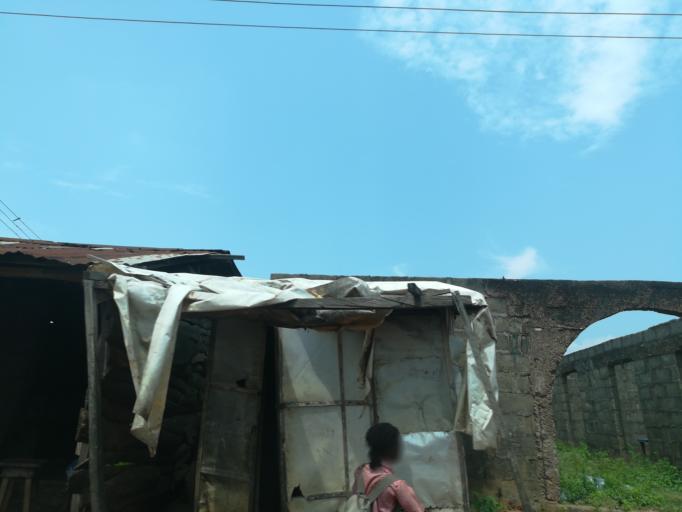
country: NG
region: Lagos
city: Ikorodu
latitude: 6.5761
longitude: 3.6291
